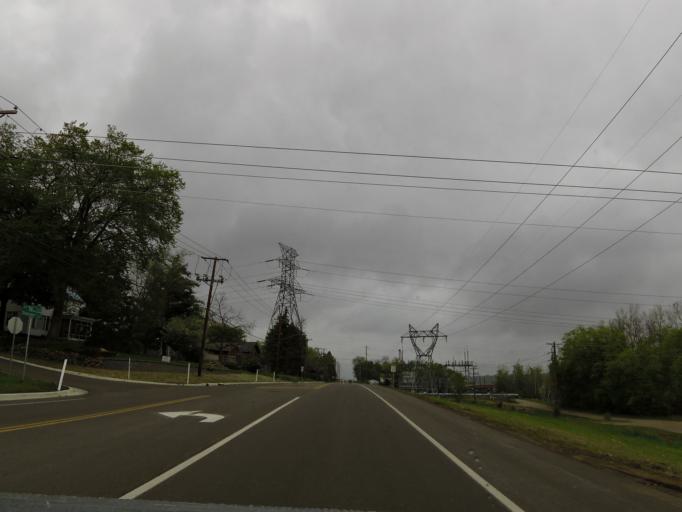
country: US
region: Minnesota
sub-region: Washington County
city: Oak Park Heights
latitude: 45.0307
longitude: -92.7912
